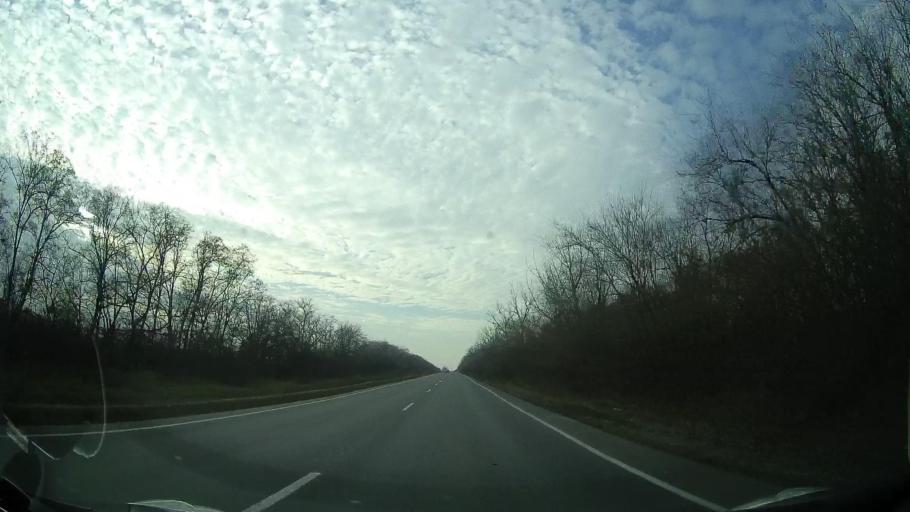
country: RU
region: Rostov
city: Bagayevskaya
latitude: 47.0961
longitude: 40.2936
